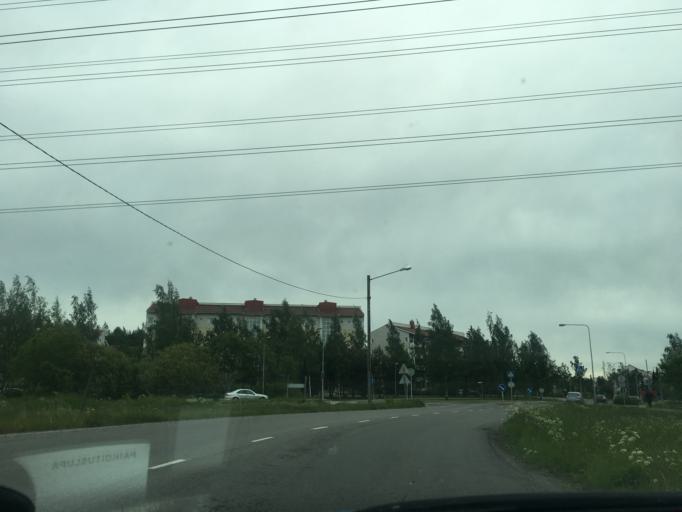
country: FI
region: Varsinais-Suomi
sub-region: Turku
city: Turku
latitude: 60.4722
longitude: 22.3085
